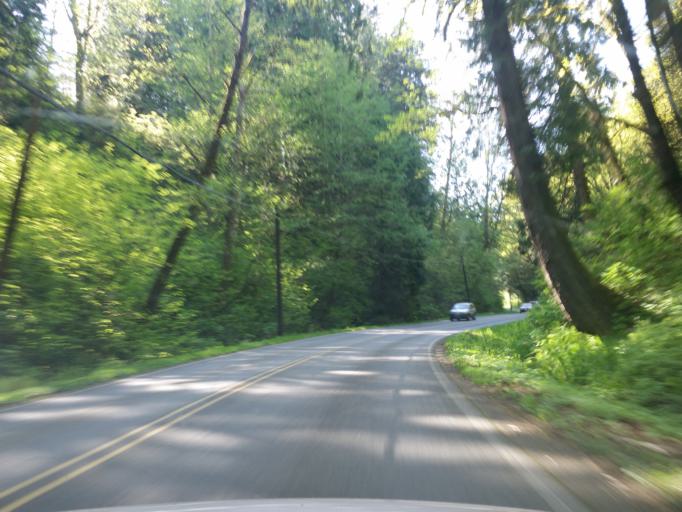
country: US
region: Washington
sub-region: Snohomish County
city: Snohomish
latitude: 47.9481
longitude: -122.0795
